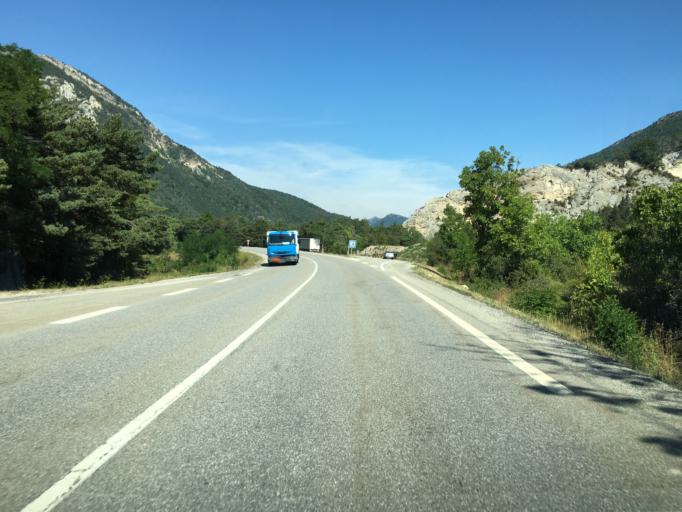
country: FR
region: Provence-Alpes-Cote d'Azur
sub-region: Departement des Hautes-Alpes
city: Veynes
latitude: 44.5924
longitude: 5.7173
